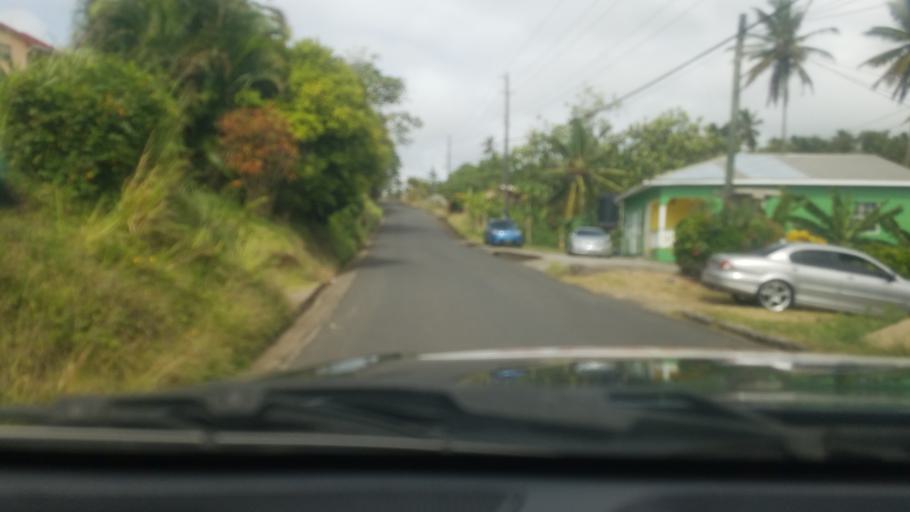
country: LC
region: Micoud Quarter
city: Micoud
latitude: 13.7970
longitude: -60.9285
